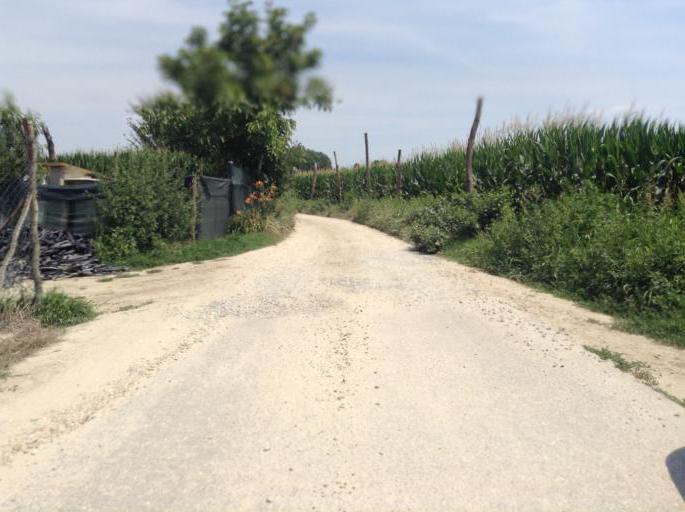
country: IT
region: Piedmont
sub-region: Provincia di Torino
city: Carignano
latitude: 44.9087
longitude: 7.6832
